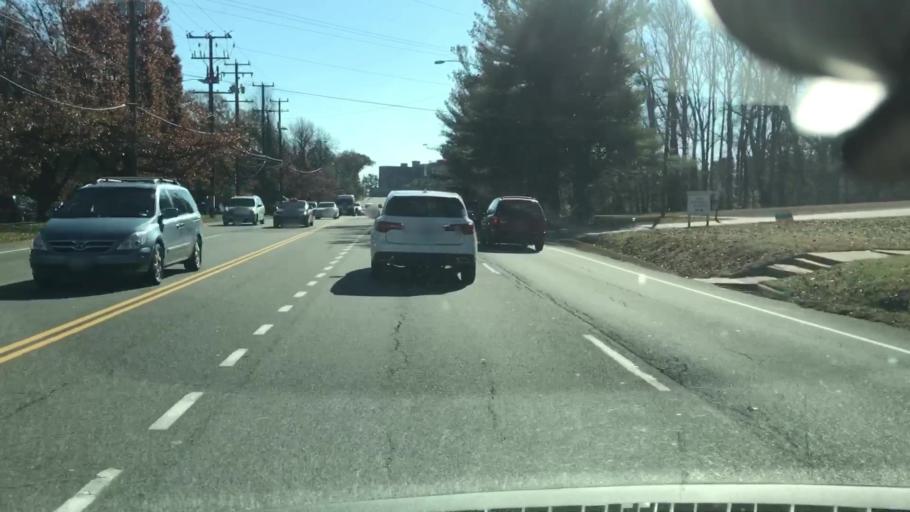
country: US
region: Virginia
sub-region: Fairfax County
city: Seven Corners
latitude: 38.8639
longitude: -77.1495
